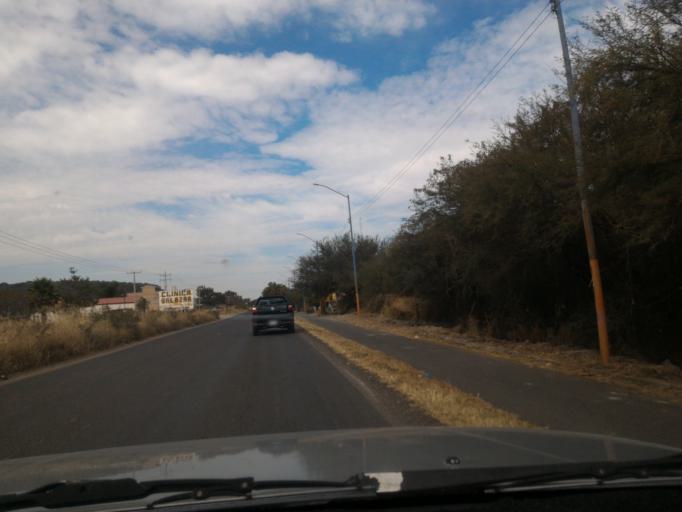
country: MX
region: Guanajuato
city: Ciudad Manuel Doblado
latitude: 20.7407
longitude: -101.9557
